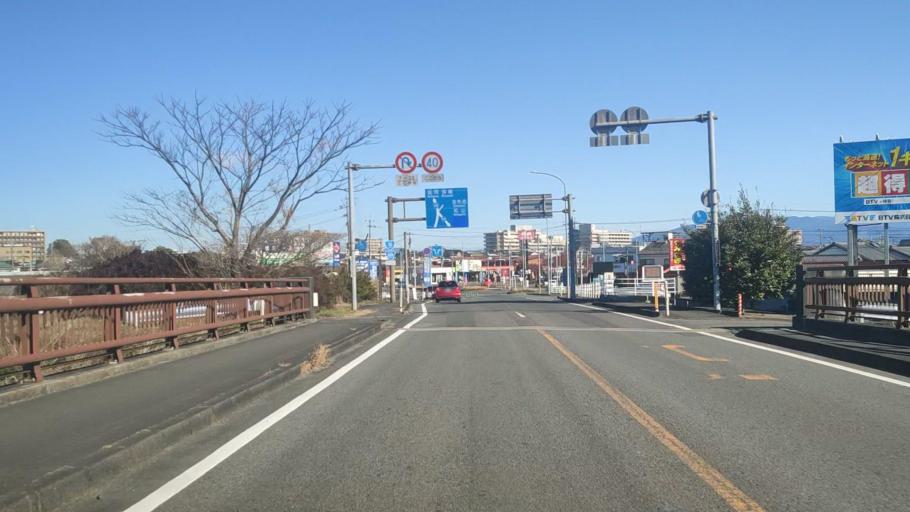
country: JP
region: Miyazaki
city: Miyakonojo
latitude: 31.7133
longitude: 131.0592
